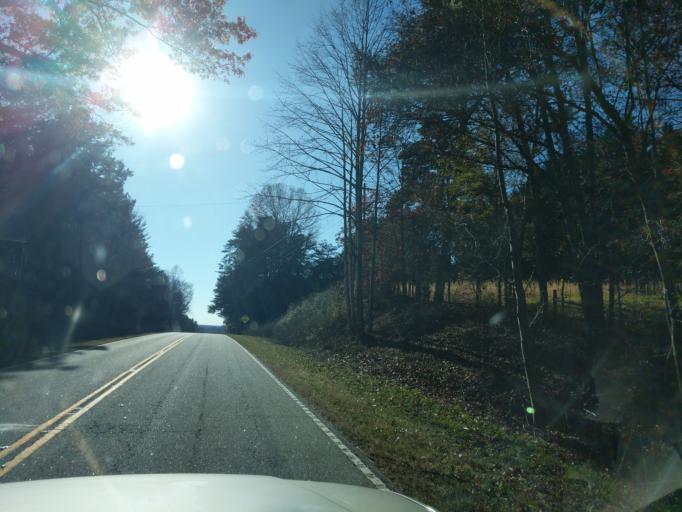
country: US
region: South Carolina
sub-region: Spartanburg County
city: Landrum
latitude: 35.1267
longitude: -82.1359
